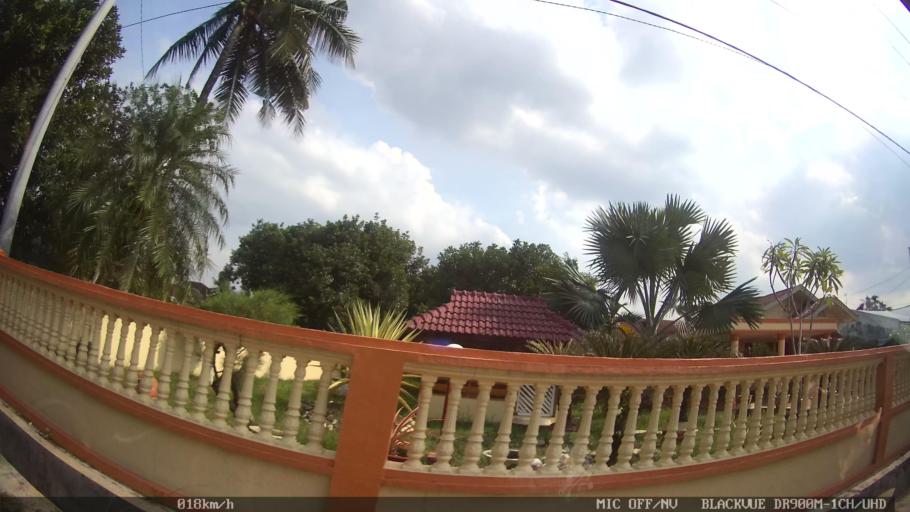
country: ID
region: North Sumatra
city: Binjai
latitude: 3.6063
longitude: 98.5012
